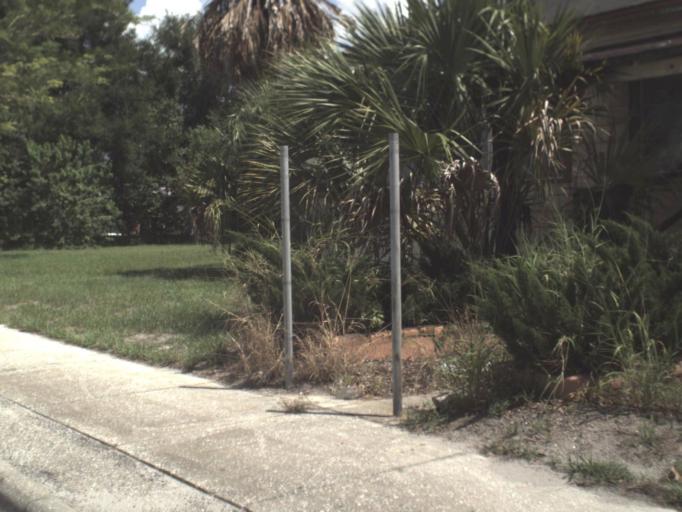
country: US
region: Florida
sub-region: Hardee County
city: Zolfo Springs
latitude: 27.4947
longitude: -81.7963
